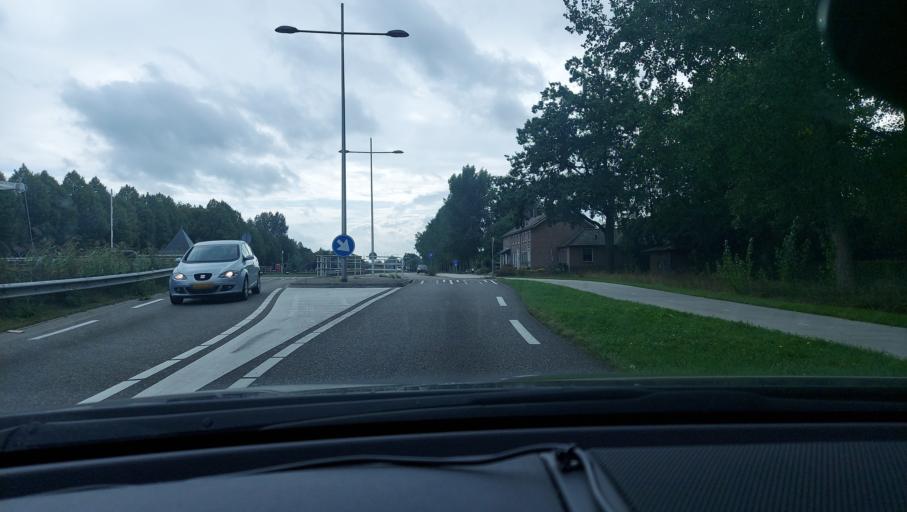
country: NL
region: North Brabant
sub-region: Gemeente Helmond
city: Helmond
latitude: 51.4968
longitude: 5.6519
